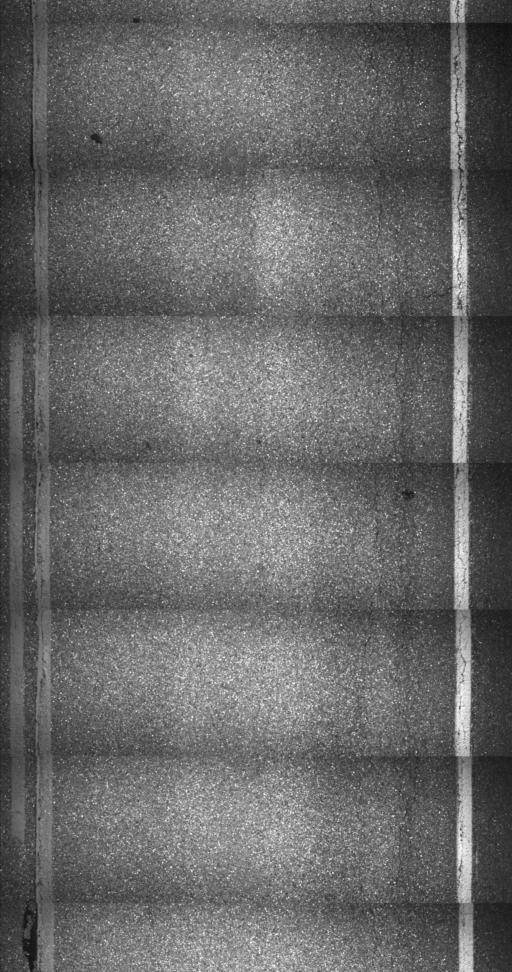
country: US
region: Vermont
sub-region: Rutland County
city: Fair Haven
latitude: 43.6539
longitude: -73.2939
